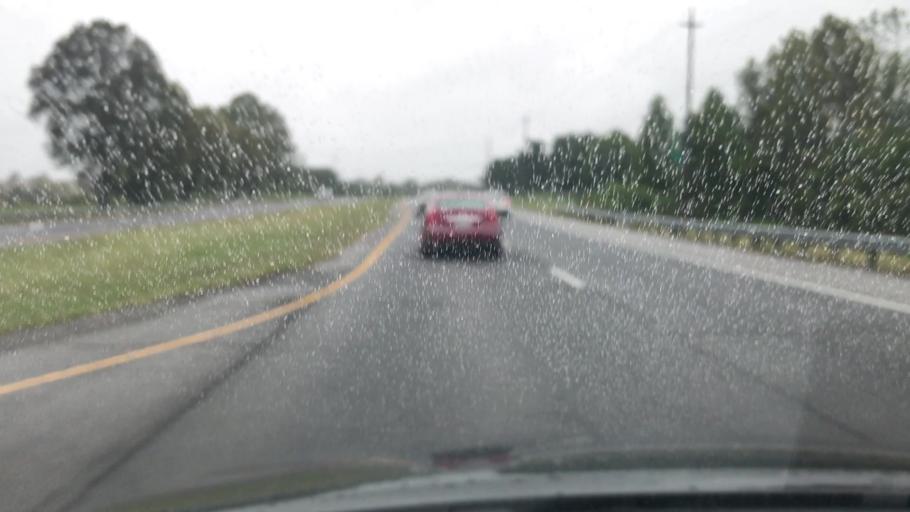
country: US
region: Tennessee
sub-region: Cheatham County
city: Ashland City
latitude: 36.2204
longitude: -86.9990
